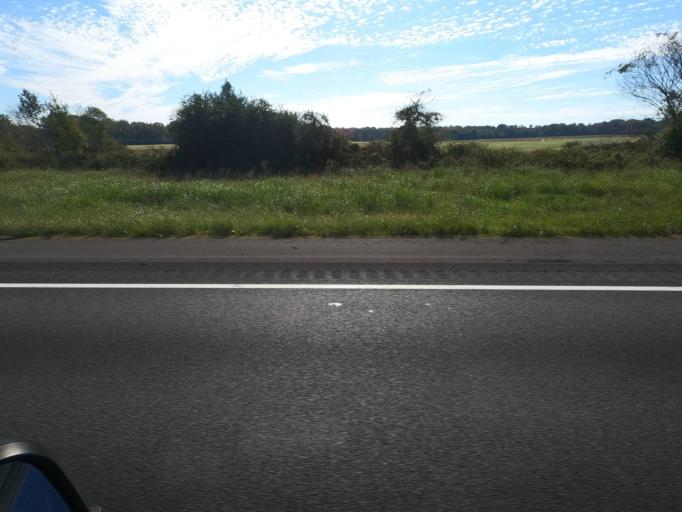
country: US
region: Tennessee
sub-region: Shelby County
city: Arlington
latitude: 35.2845
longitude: -89.6222
